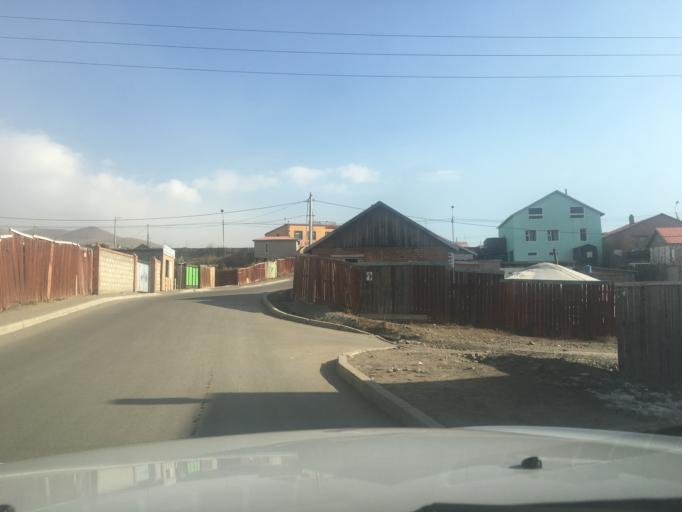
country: MN
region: Ulaanbaatar
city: Ulaanbaatar
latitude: 47.9651
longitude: 106.8277
